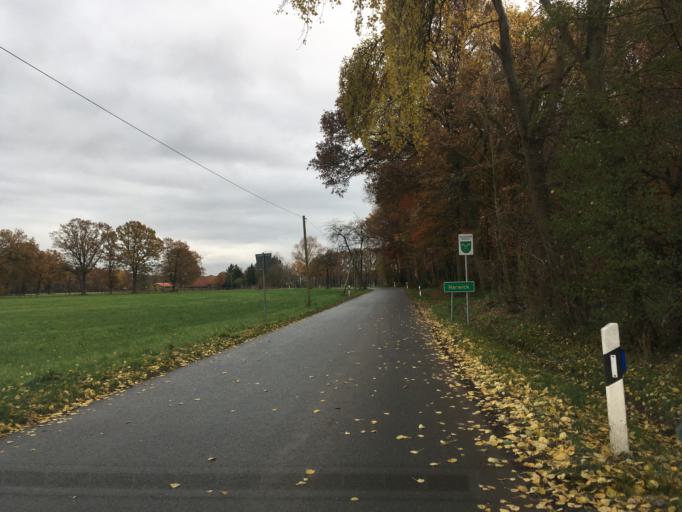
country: DE
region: North Rhine-Westphalia
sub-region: Regierungsbezirk Munster
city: Gescher
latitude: 51.9818
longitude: 6.9904
